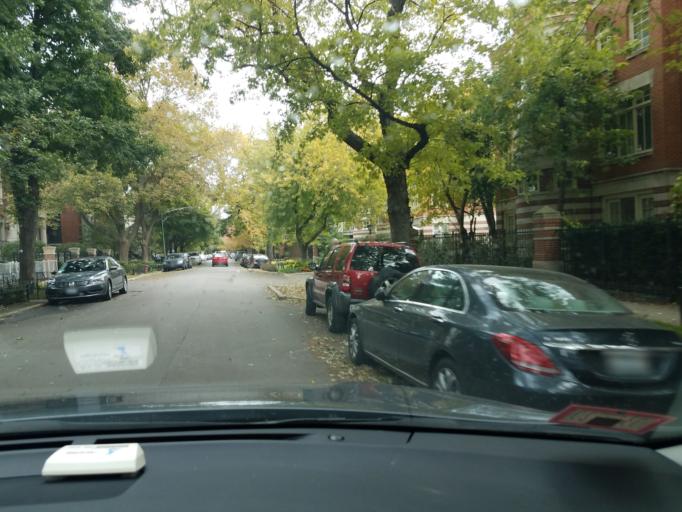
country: US
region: Illinois
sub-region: Cook County
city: Chicago
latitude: 41.9297
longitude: -87.6659
